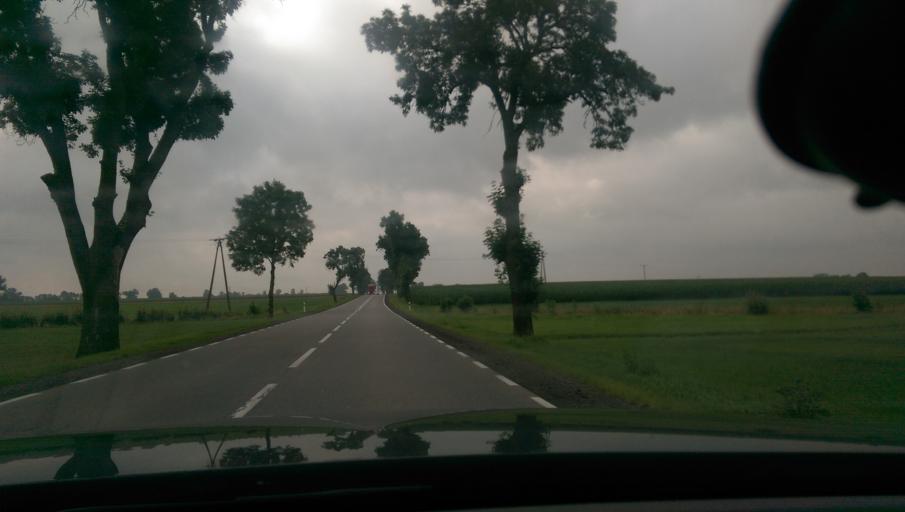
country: PL
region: Masovian Voivodeship
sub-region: Powiat przasnyski
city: Przasnysz
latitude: 53.0641
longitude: 20.8653
